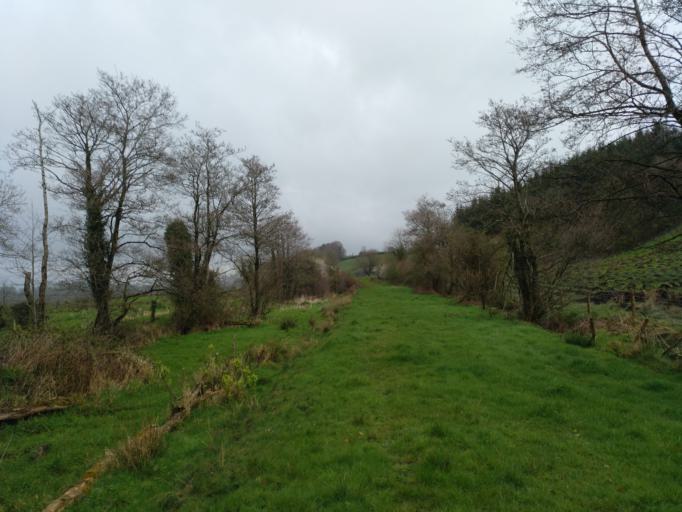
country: IE
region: Ulster
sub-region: County Monaghan
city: Clones
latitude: 54.1827
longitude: -7.1929
